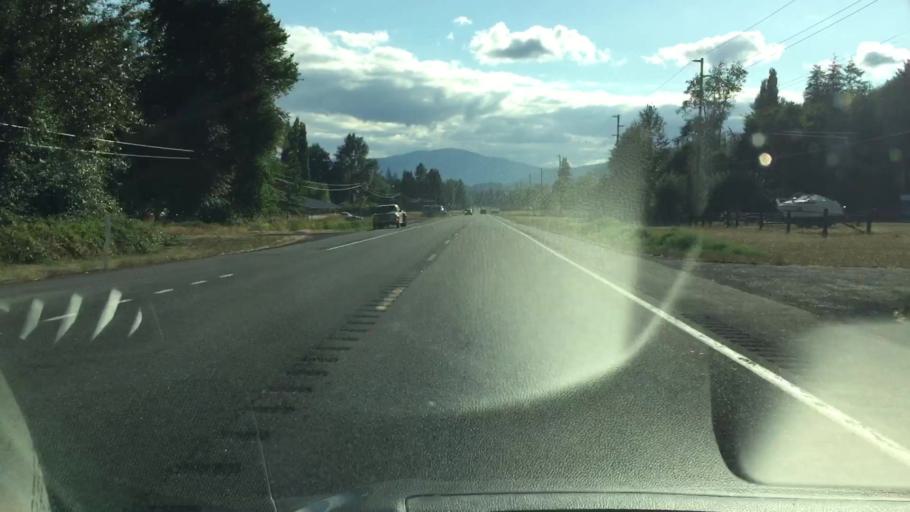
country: US
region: Washington
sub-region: Lewis County
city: Morton
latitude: 46.5327
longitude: -122.1258
